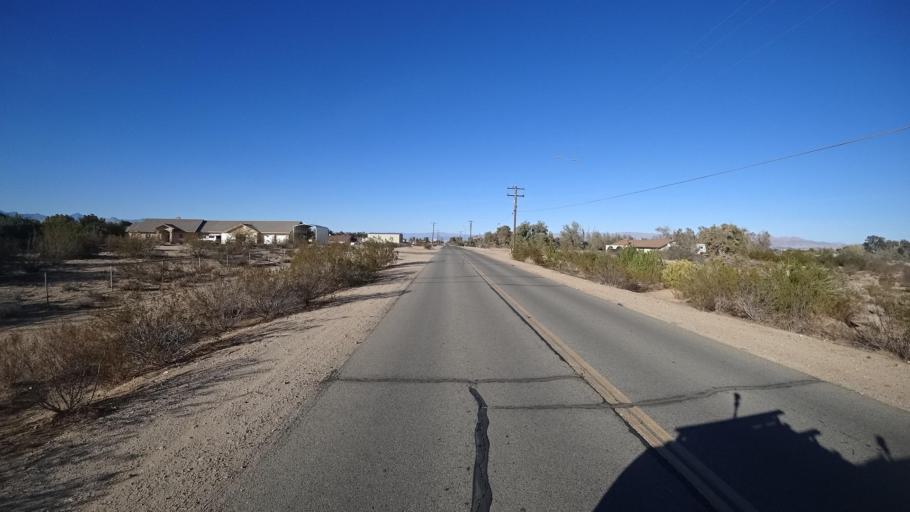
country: US
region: California
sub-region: Kern County
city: Ridgecrest
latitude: 35.6303
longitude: -117.7056
